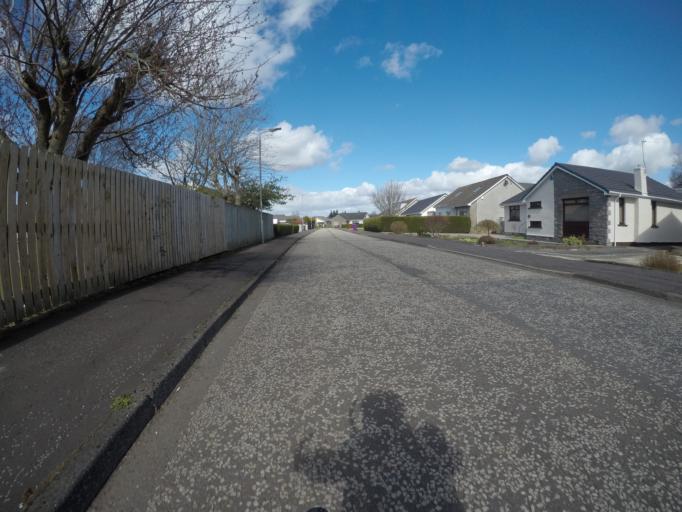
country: GB
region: Scotland
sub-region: North Ayrshire
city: Irvine
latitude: 55.6163
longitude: -4.6480
